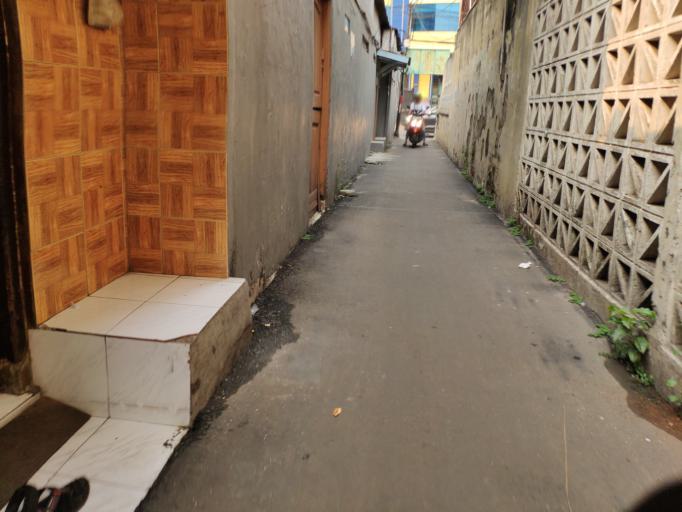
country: ID
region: Jakarta Raya
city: Jakarta
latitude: -6.1939
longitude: 106.8674
